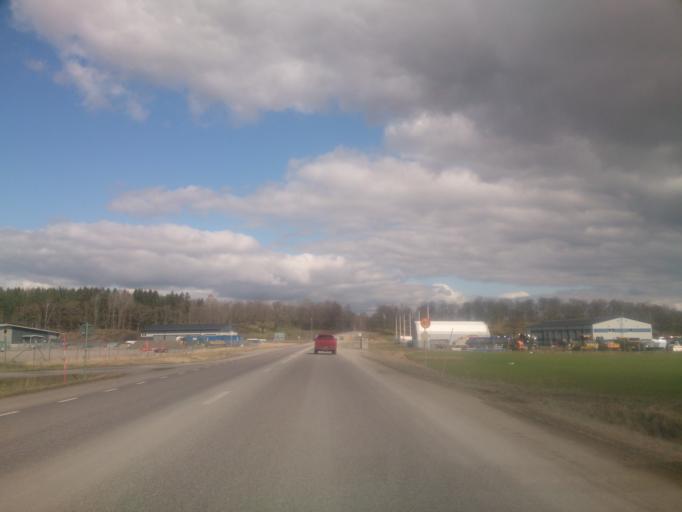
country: SE
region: OEstergoetland
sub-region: Norrkopings Kommun
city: Norrkoping
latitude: 58.5655
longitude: 16.0815
